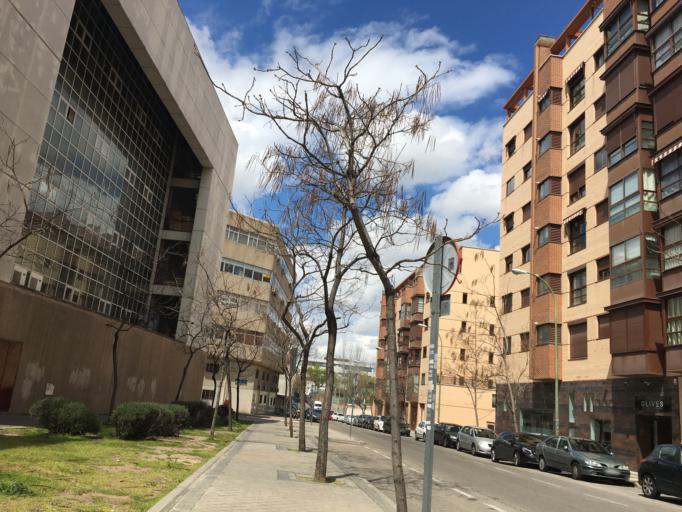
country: ES
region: Madrid
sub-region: Provincia de Madrid
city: San Blas
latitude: 40.4334
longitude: -3.6258
